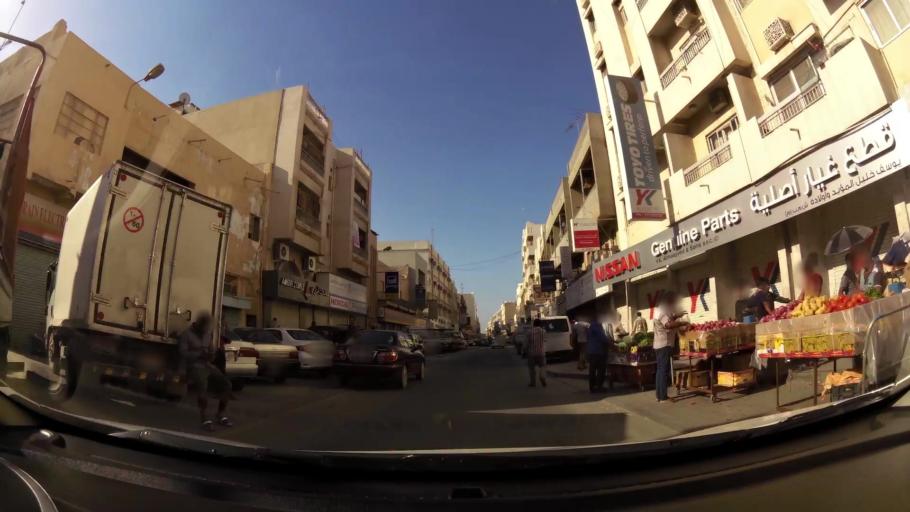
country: BH
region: Manama
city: Manama
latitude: 26.2254
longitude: 50.5722
